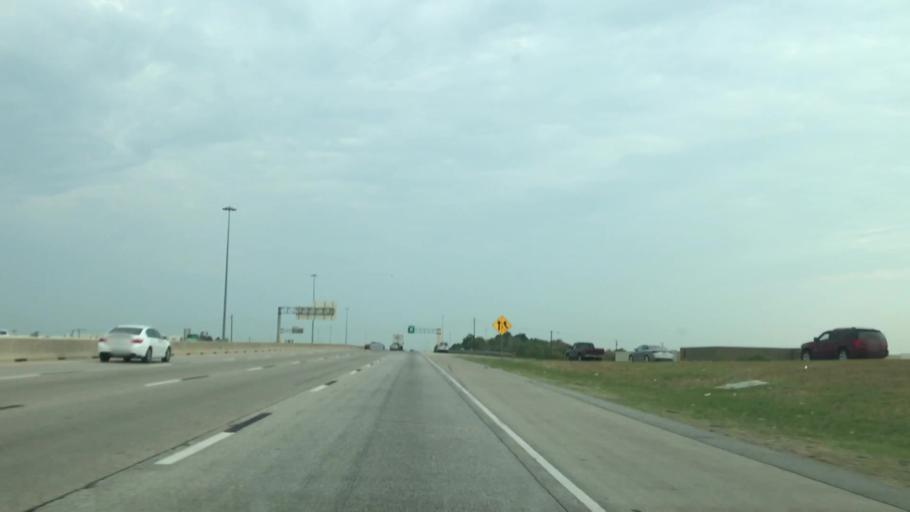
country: US
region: Texas
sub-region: Dallas County
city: Cockrell Hill
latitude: 32.7668
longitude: -96.8980
